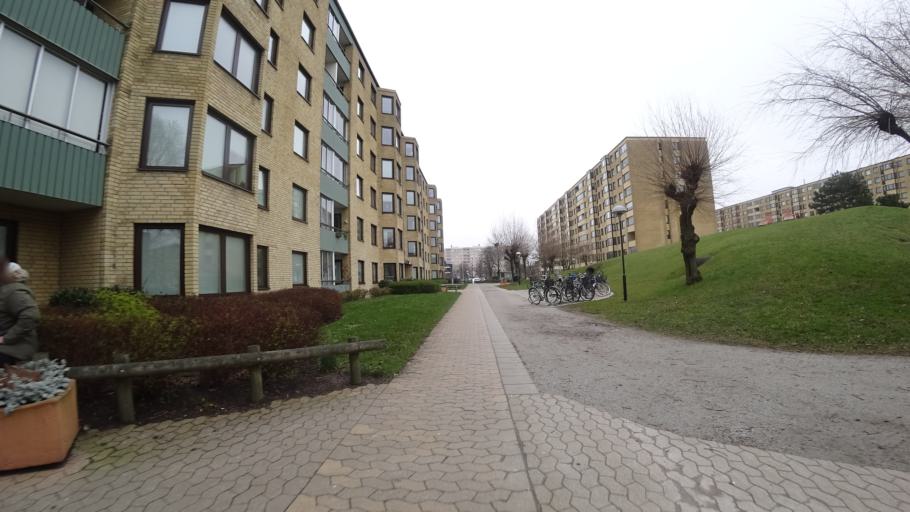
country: SE
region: Skane
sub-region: Malmo
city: Malmoe
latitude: 55.5825
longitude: 12.9749
